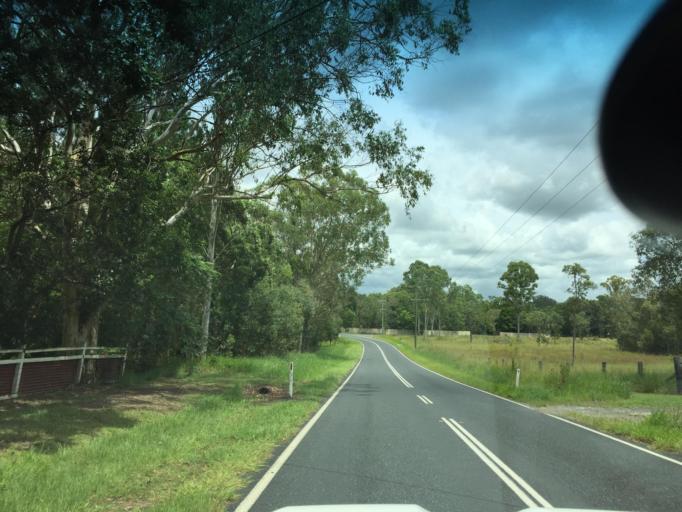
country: AU
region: Queensland
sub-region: Moreton Bay
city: Caboolture
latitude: -27.0456
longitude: 152.9137
